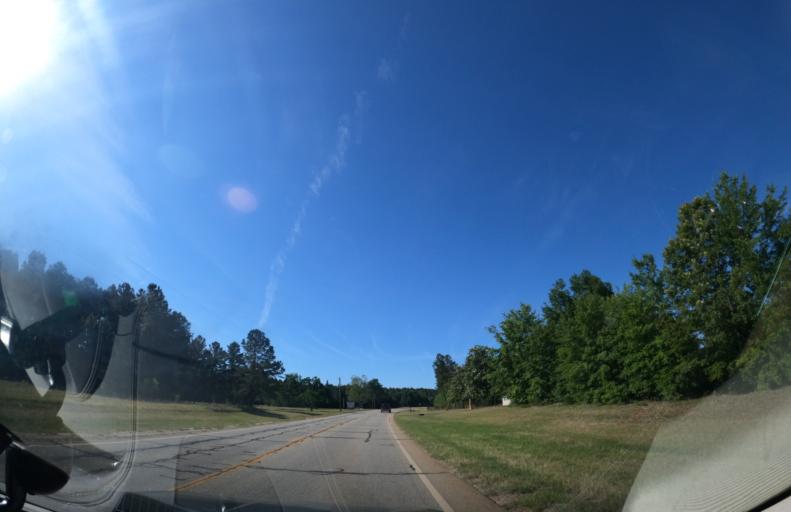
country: US
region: Georgia
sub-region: Jefferson County
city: Wrens
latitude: 33.2638
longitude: -82.3844
